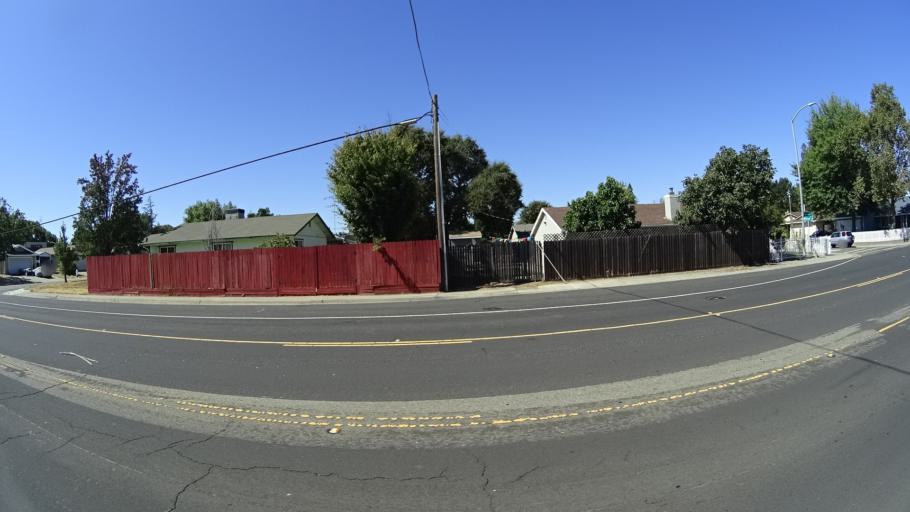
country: US
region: California
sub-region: Sacramento County
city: Elk Grove
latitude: 38.4058
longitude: -121.3530
